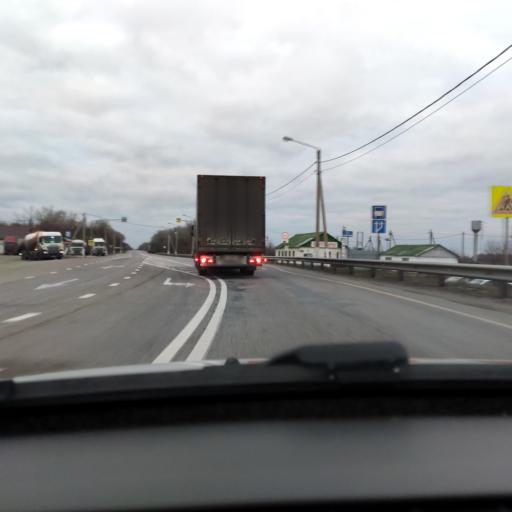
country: RU
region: Lipetsk
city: Khlevnoye
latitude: 52.2671
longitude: 39.1687
